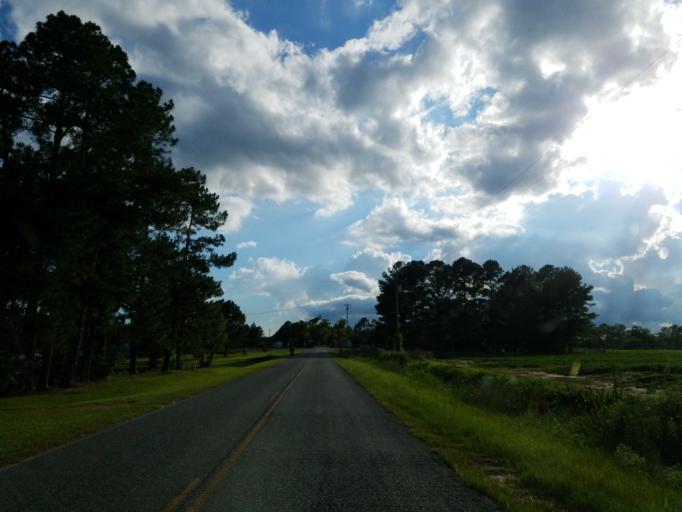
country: US
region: Georgia
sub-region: Turner County
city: Ashburn
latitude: 31.6196
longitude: -83.6042
